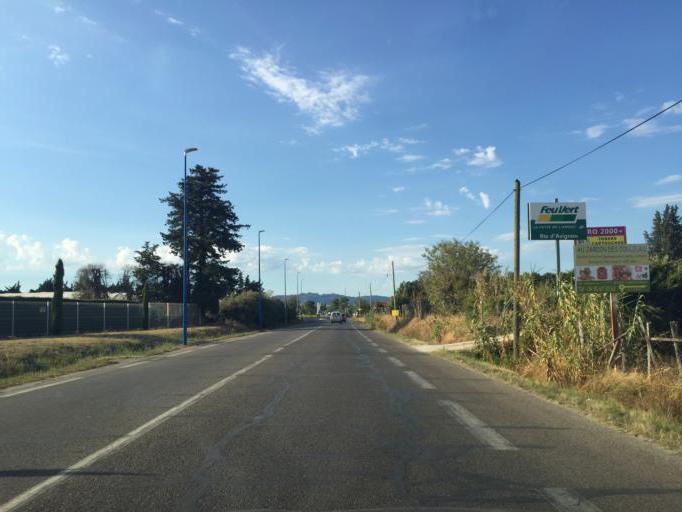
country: FR
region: Provence-Alpes-Cote d'Azur
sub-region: Departement du Vaucluse
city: Carpentras
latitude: 44.0303
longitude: 5.0521
